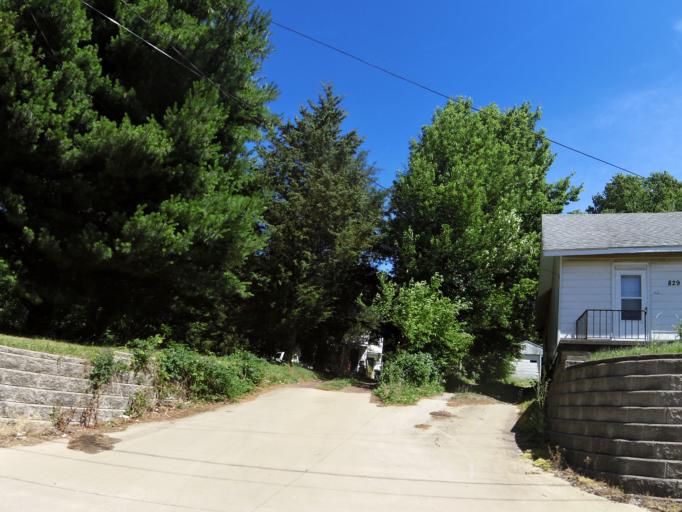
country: US
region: Illinois
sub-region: Vermilion County
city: Danville
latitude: 40.1257
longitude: -87.6143
